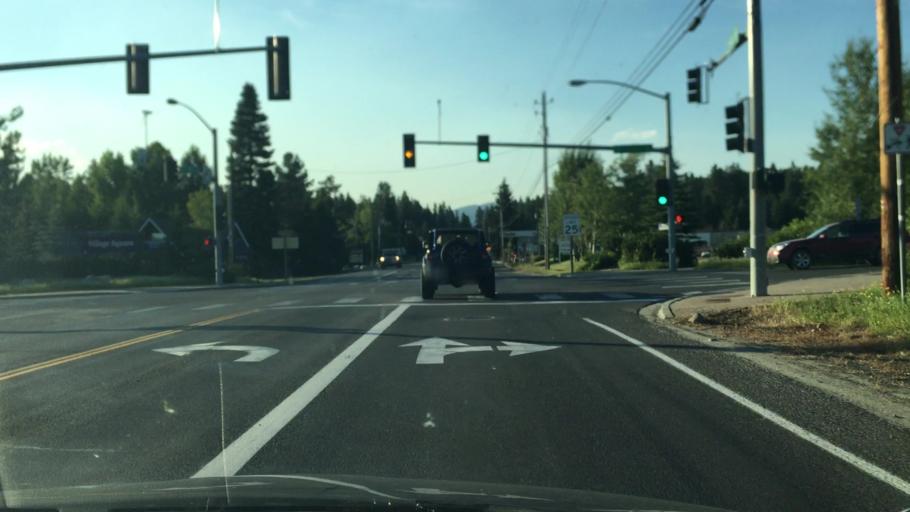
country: US
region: Idaho
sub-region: Valley County
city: McCall
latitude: 44.8975
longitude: -116.0964
